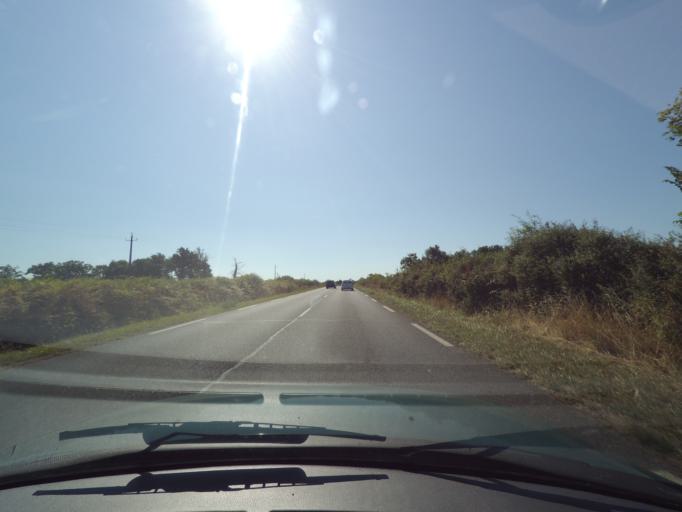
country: FR
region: Limousin
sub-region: Departement de la Haute-Vienne
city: Peyrat-de-Bellac
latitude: 46.1456
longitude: 0.9711
